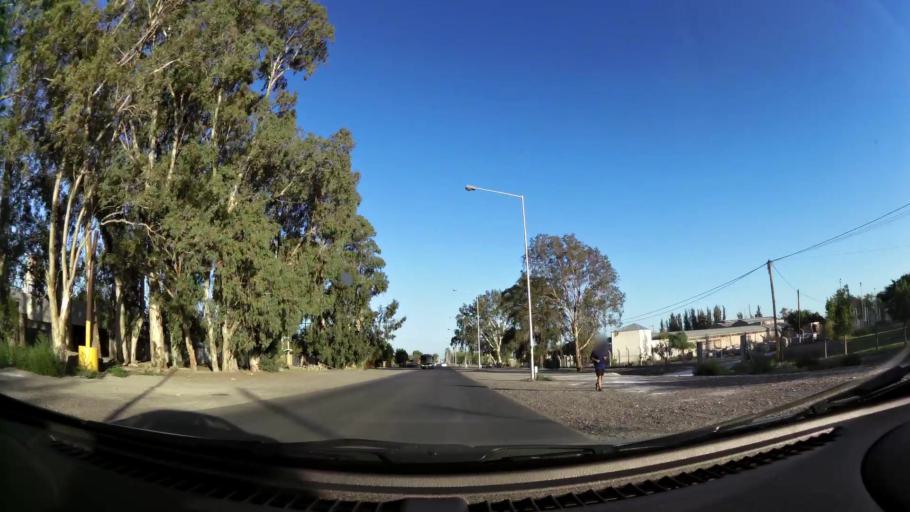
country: AR
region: San Juan
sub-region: Departamento de Santa Lucia
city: Santa Lucia
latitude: -31.5475
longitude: -68.4861
